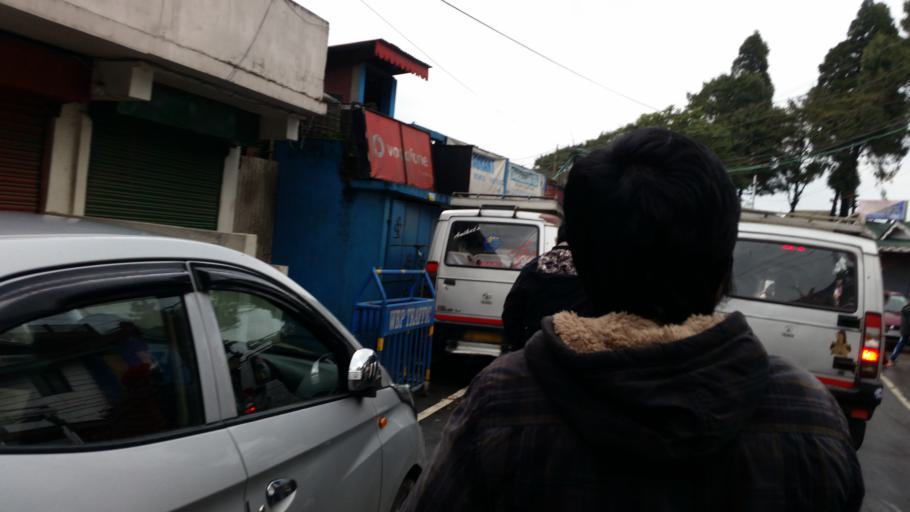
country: IN
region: West Bengal
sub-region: Darjiling
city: Darjiling
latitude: 27.0160
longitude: 88.2477
